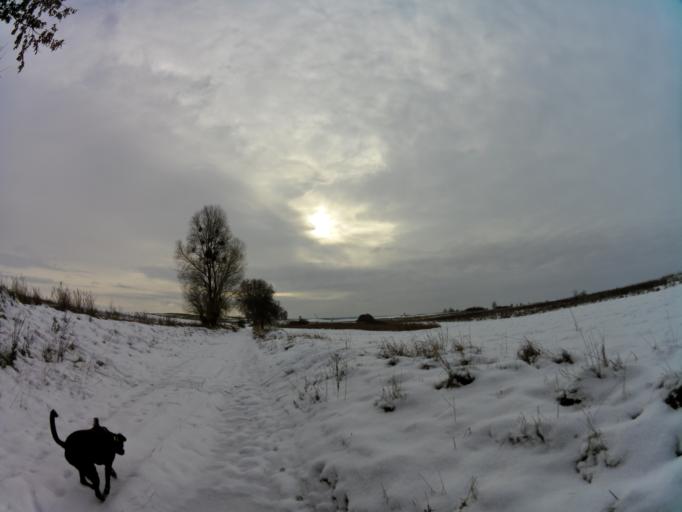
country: PL
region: West Pomeranian Voivodeship
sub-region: Powiat choszczenski
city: Recz
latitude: 53.2860
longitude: 15.5069
